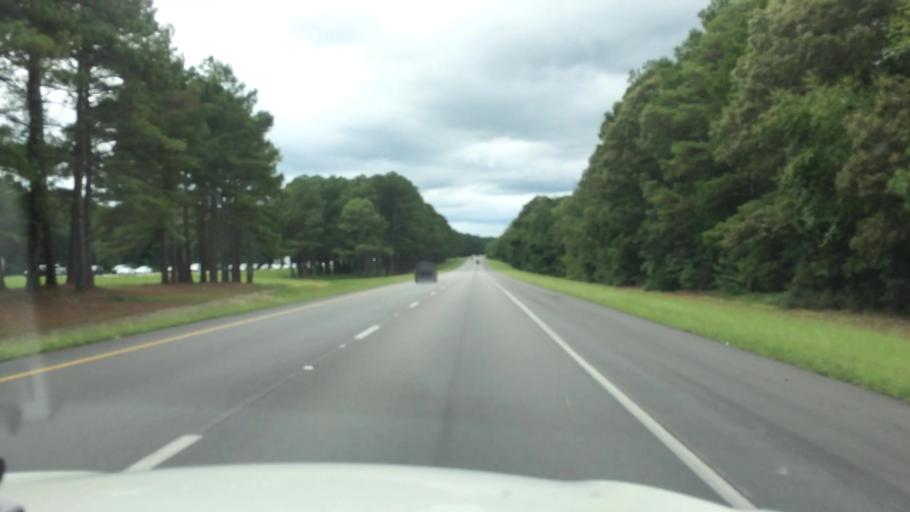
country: US
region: South Carolina
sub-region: Lee County
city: Bishopville
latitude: 34.1956
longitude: -80.3182
